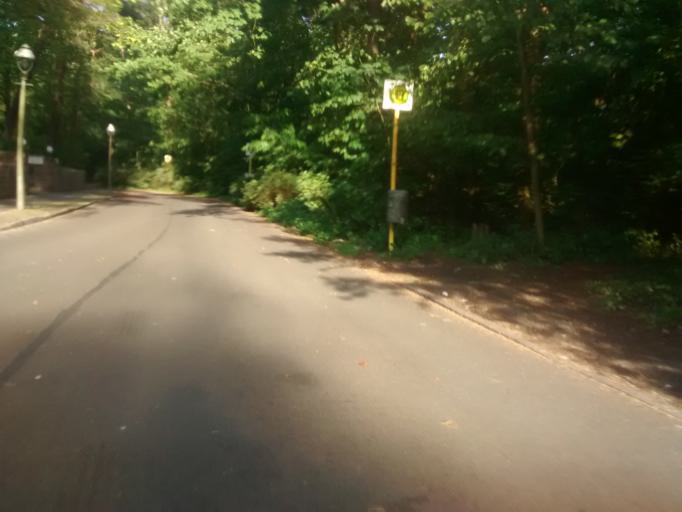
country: DE
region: Brandenburg
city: Hohen Neuendorf
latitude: 52.6550
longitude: 13.2834
